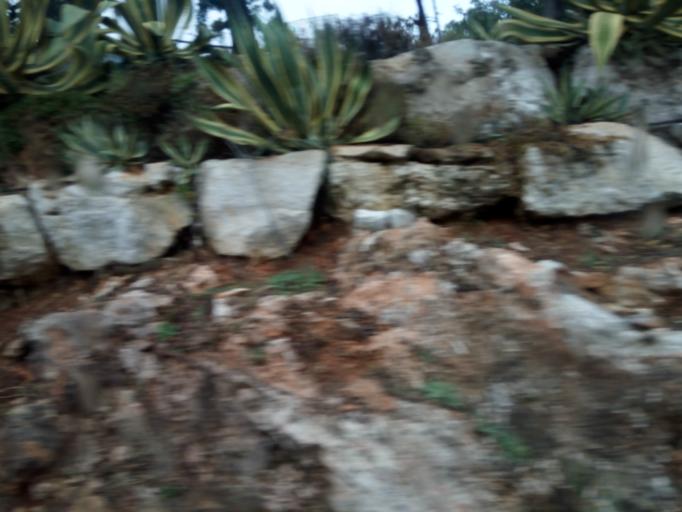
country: PT
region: Faro
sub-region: Faro
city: Santa Barbara de Nexe
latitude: 37.1045
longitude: -7.9871
